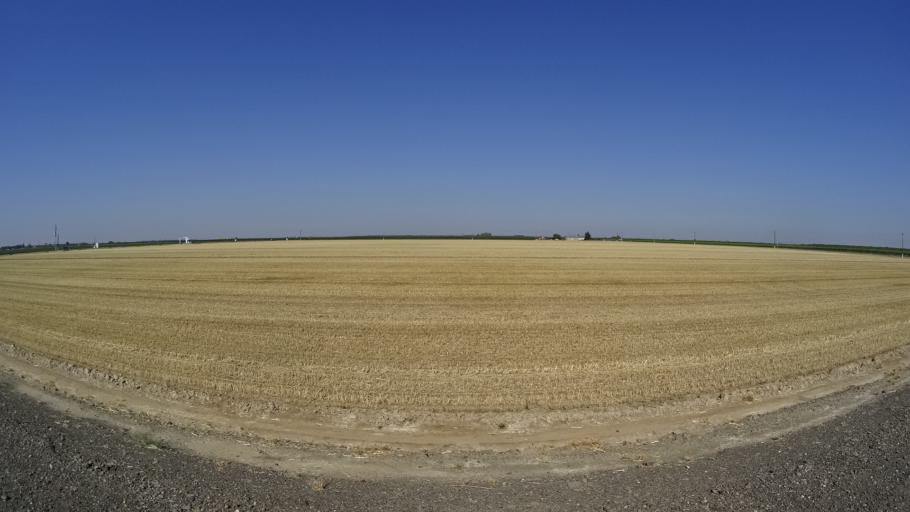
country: US
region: California
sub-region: Kings County
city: Hanford
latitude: 36.3850
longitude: -119.5650
